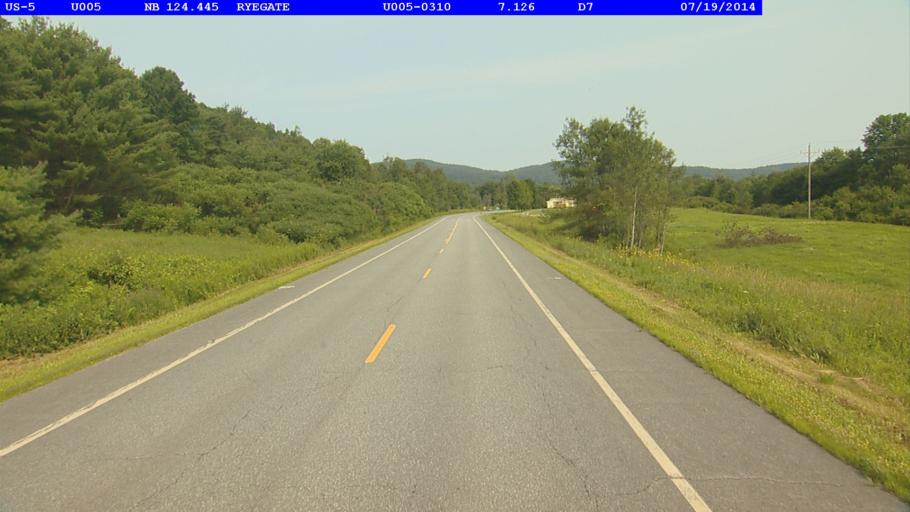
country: US
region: New Hampshire
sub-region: Grafton County
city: Woodsville
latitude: 44.2533
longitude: -72.0593
